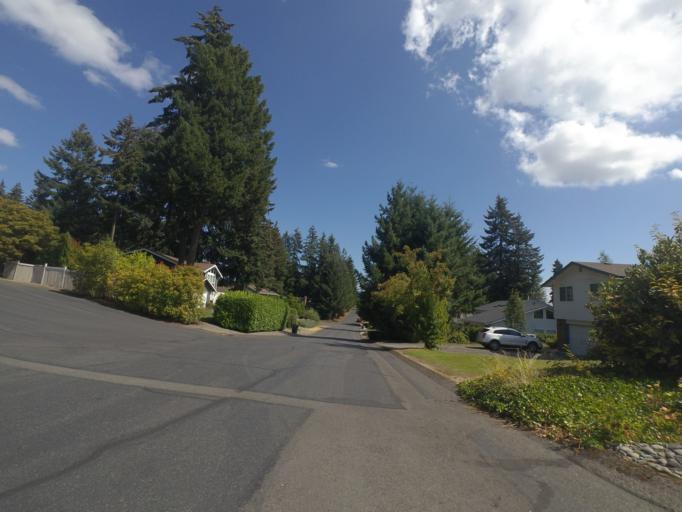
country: US
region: Washington
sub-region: Pierce County
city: Fircrest
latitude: 47.2104
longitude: -122.5191
